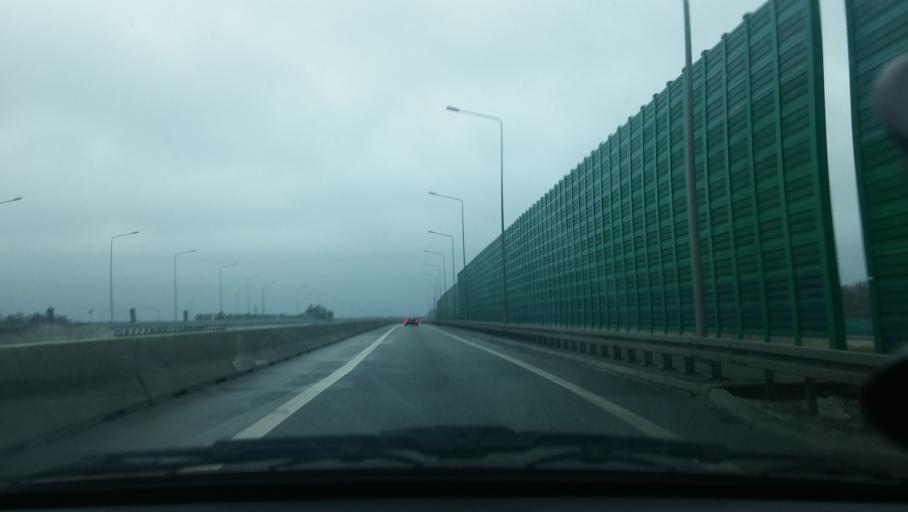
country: PL
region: Masovian Voivodeship
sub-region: Powiat minski
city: Kaluszyn
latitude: 52.1991
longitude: 21.7698
